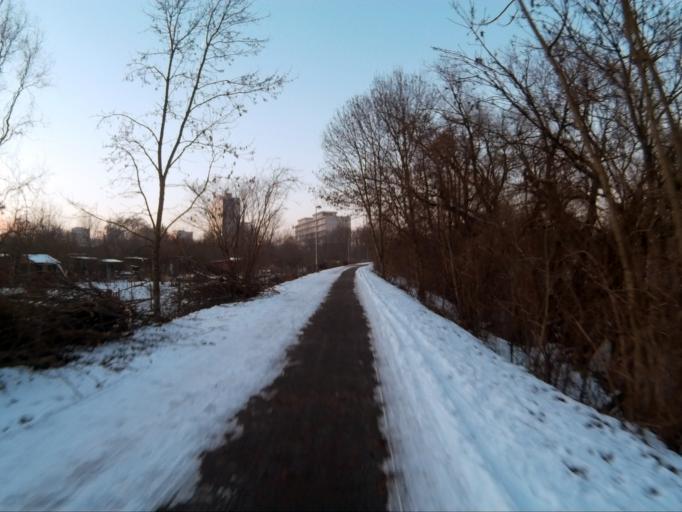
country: CZ
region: South Moravian
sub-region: Mesto Brno
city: Brno
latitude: 49.1796
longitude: 16.6125
